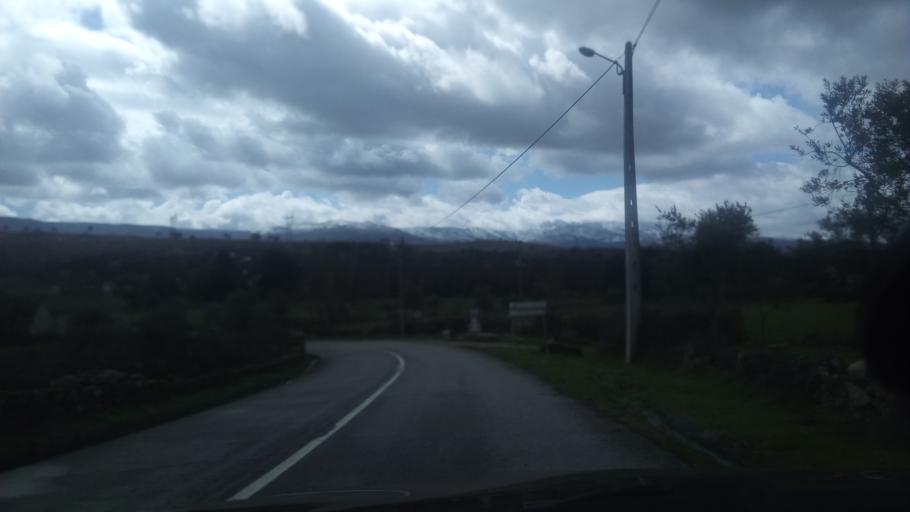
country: PT
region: Guarda
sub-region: Fornos de Algodres
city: Fornos de Algodres
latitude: 40.5911
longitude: -7.4936
